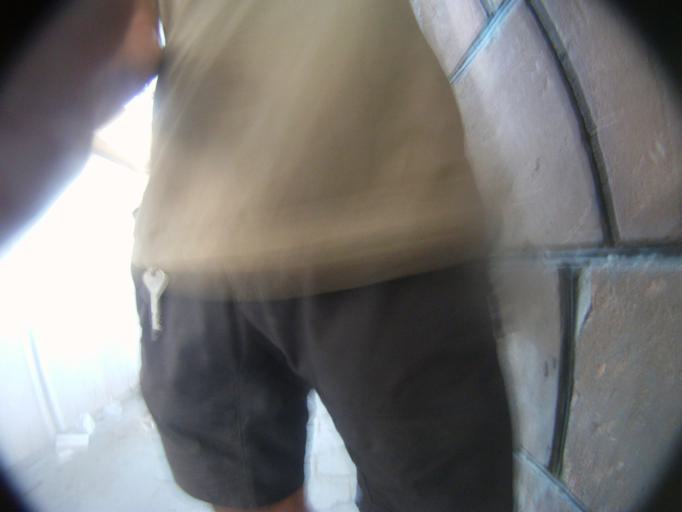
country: KZ
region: Ongtustik Qazaqstan
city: Turkestan
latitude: 43.3009
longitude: 68.2458
